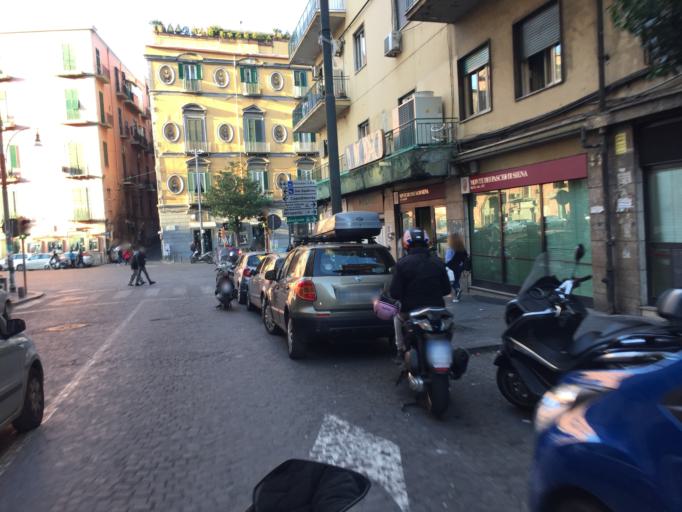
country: IT
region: Campania
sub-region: Provincia di Napoli
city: Napoli
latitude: 40.8554
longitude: 14.2573
